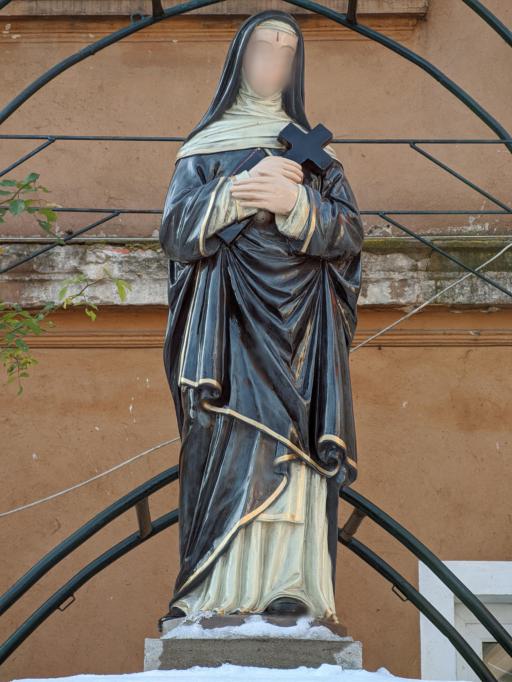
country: PL
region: Lubusz
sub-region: Powiat nowosolski
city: Nowe Miasteczko
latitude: 51.6908
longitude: 15.7297
